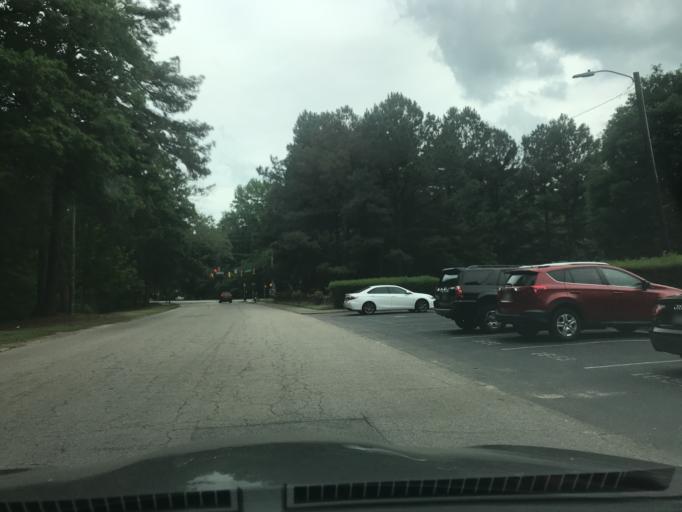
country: US
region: North Carolina
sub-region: Wake County
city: West Raleigh
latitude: 35.7900
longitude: -78.6567
